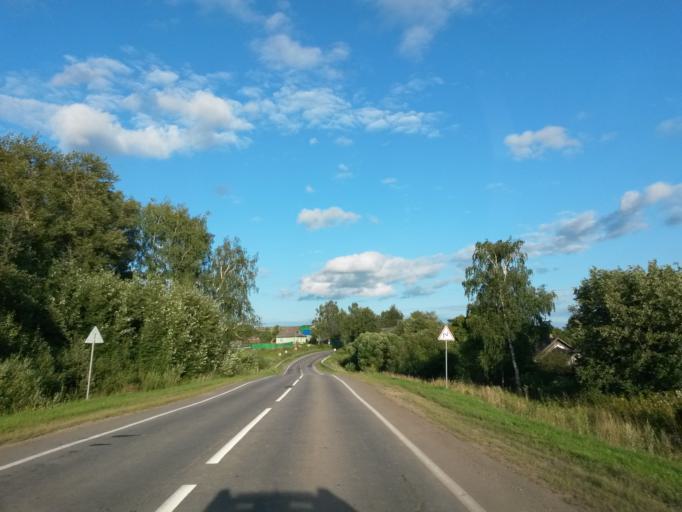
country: RU
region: Jaroslavl
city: Konstantinovskiy
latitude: 57.8474
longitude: 39.6357
